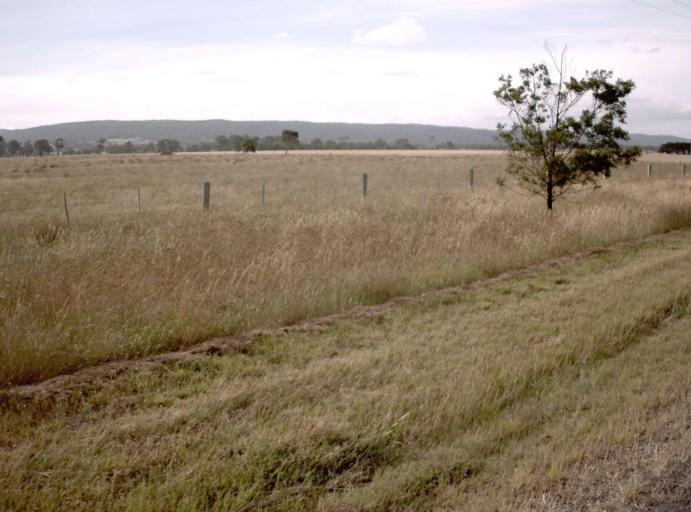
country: AU
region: Victoria
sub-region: Wellington
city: Heyfield
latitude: -38.0562
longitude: 146.6626
